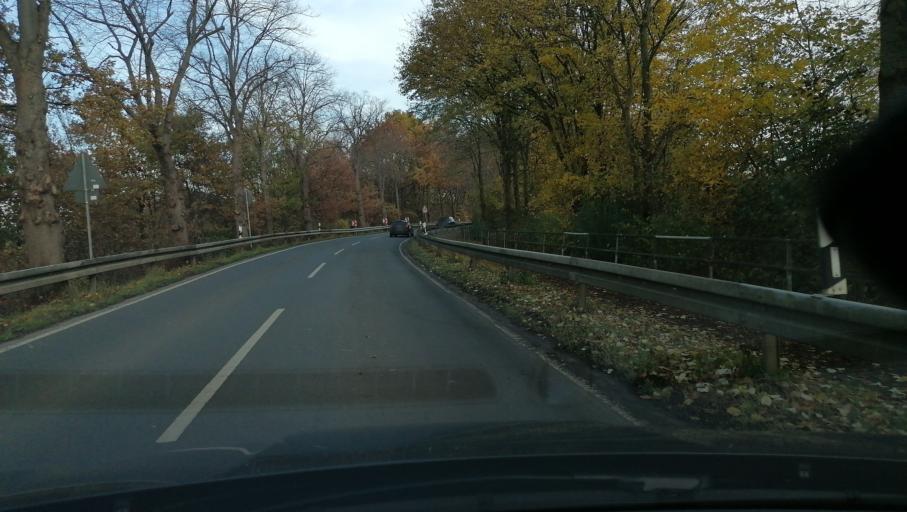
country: DE
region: North Rhine-Westphalia
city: Castrop-Rauxel
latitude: 51.5824
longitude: 7.2866
